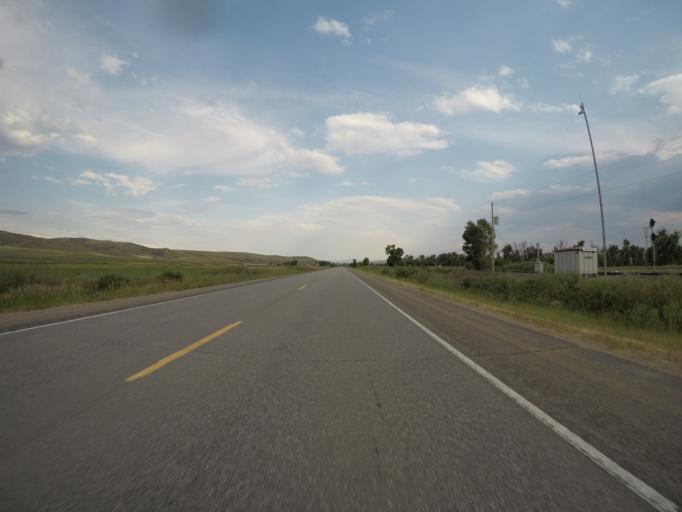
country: US
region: Colorado
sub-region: Routt County
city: Hayden
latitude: 40.5191
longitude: -107.3975
